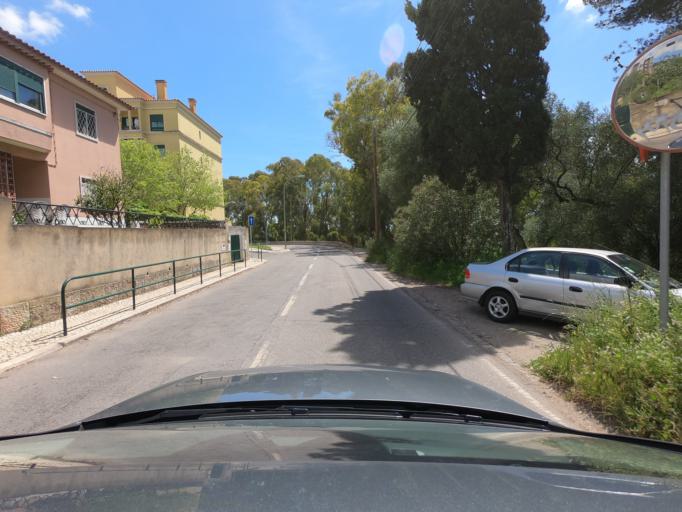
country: PT
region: Lisbon
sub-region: Oeiras
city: Linda-a-Velha
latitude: 38.7046
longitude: -9.2526
